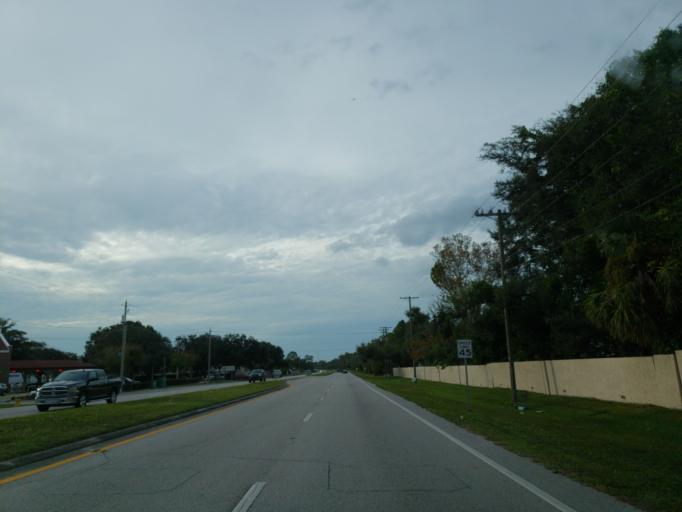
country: US
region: Florida
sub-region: Hillsborough County
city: Carrollwood Village
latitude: 28.0524
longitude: -82.5239
